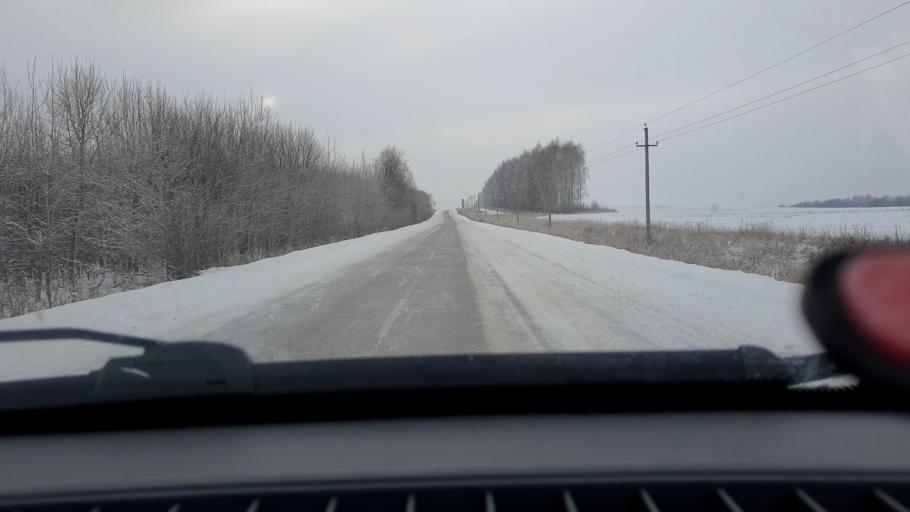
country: RU
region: Bashkortostan
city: Iglino
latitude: 54.6650
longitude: 56.4222
